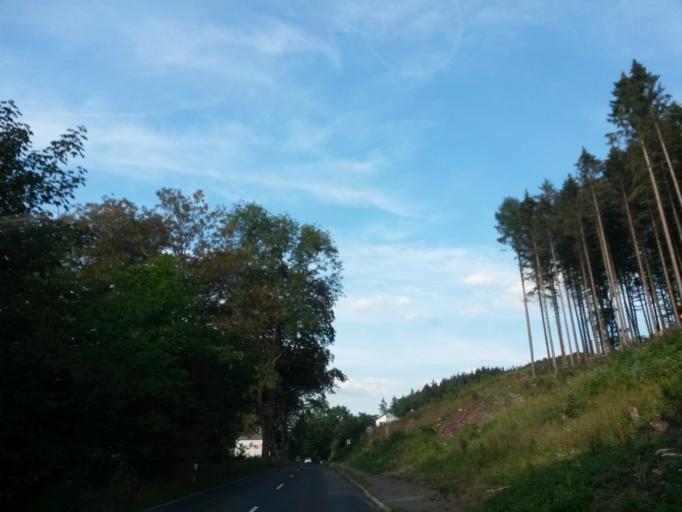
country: DE
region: North Rhine-Westphalia
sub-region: Regierungsbezirk Koln
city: Lindlar
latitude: 51.0427
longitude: 7.4478
